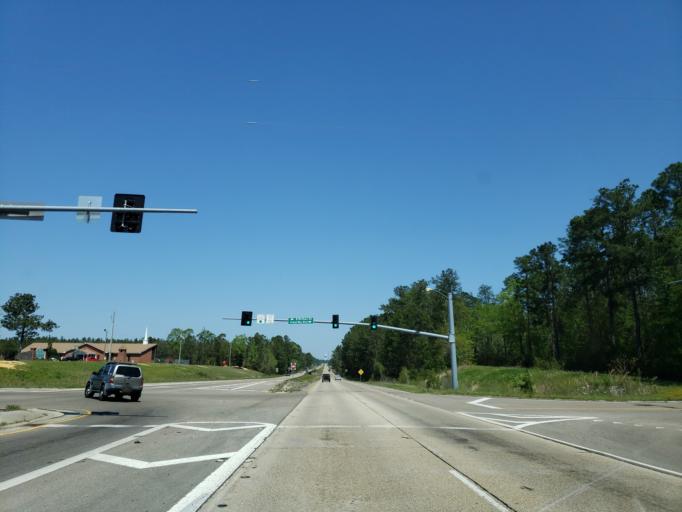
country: US
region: Mississippi
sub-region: Harrison County
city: Lyman
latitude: 30.5550
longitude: -89.1212
